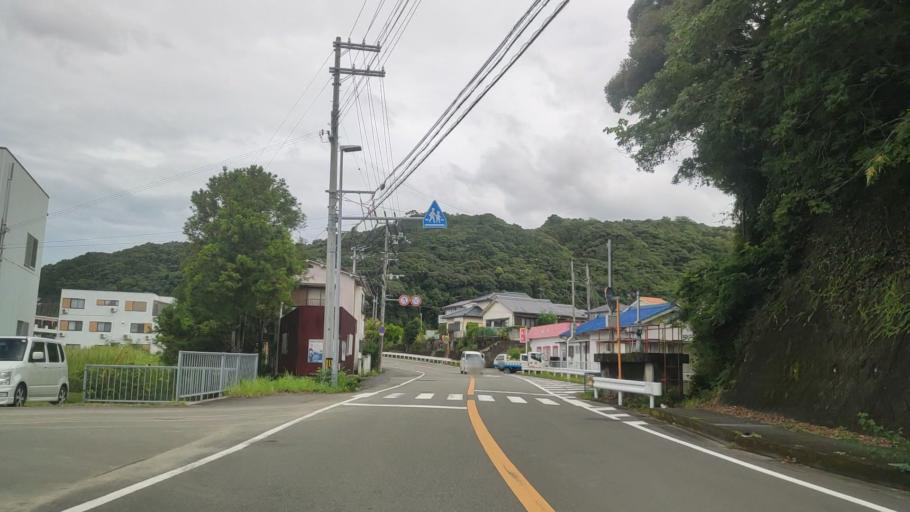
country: JP
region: Wakayama
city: Tanabe
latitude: 33.6708
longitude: 135.3882
